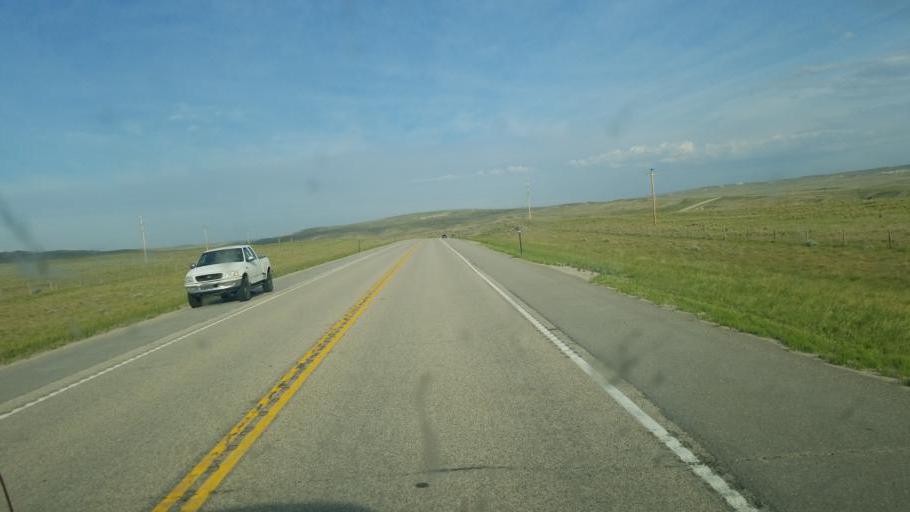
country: US
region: Wyoming
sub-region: Natrona County
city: Mills
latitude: 43.0335
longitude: -107.0104
